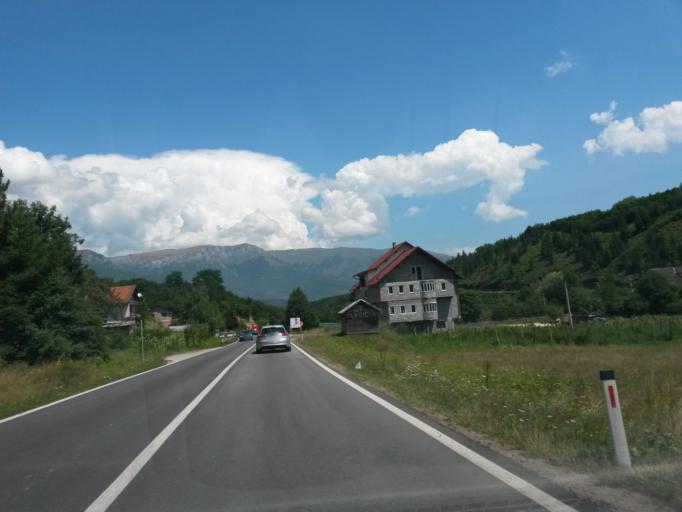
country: BA
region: Federation of Bosnia and Herzegovina
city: Turbe
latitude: 44.2278
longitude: 17.5546
